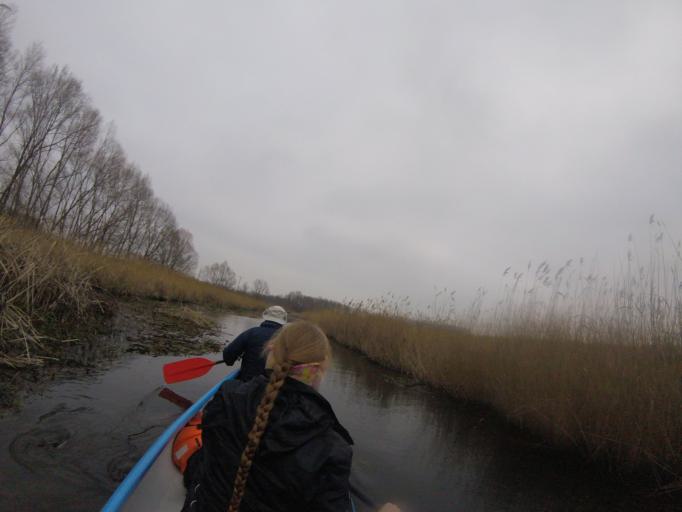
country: HU
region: Zala
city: Keszthely
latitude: 46.7587
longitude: 17.2078
